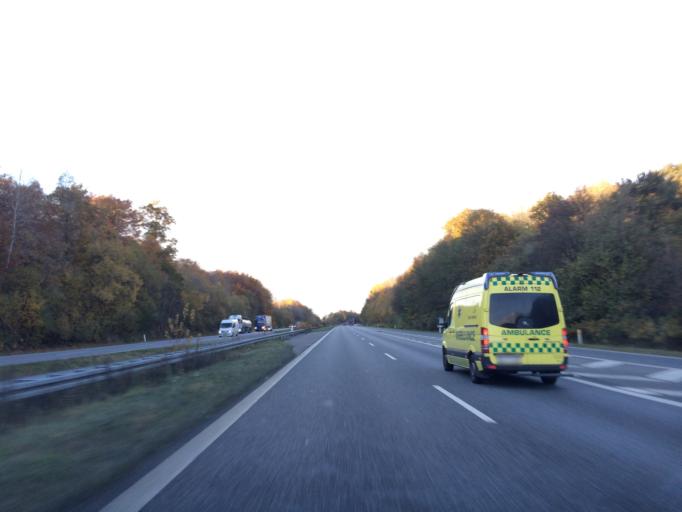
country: DK
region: South Denmark
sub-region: Aabenraa Kommune
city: Aabenraa
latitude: 55.0027
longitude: 9.3671
